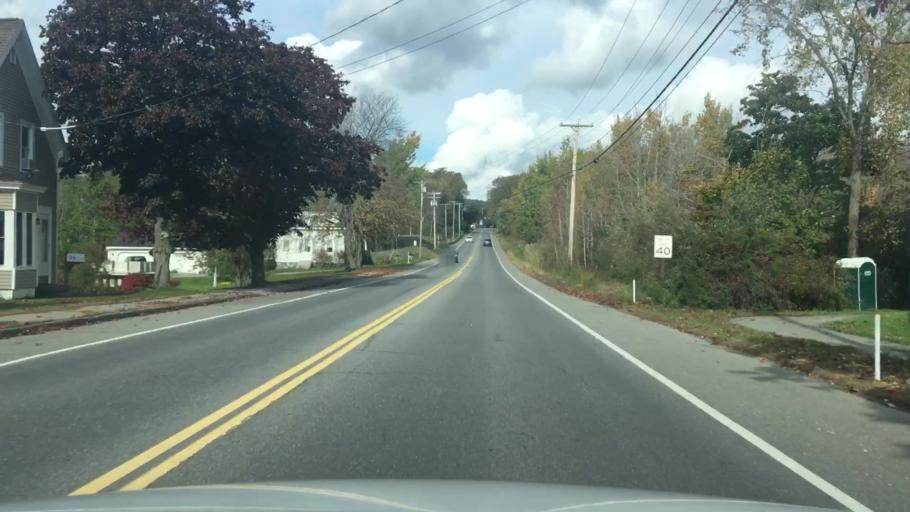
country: US
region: Maine
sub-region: Knox County
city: Rockland
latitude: 44.1205
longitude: -69.1128
